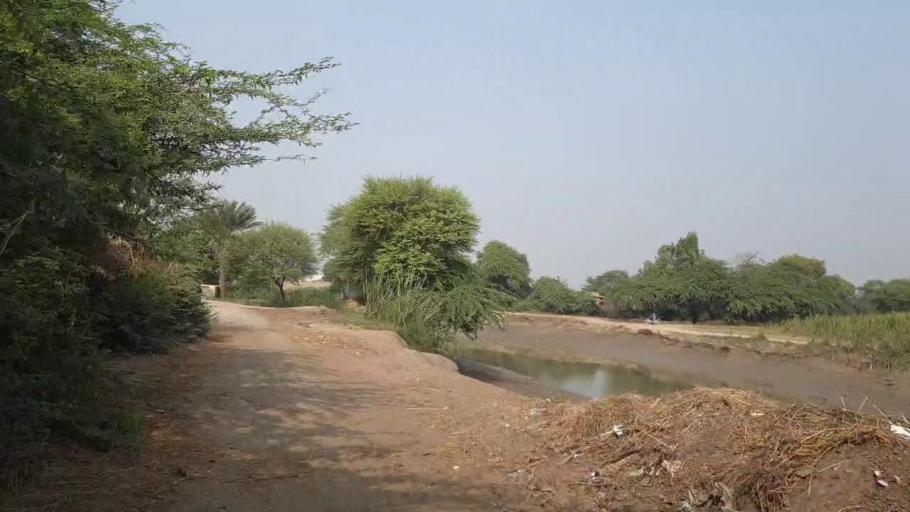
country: PK
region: Sindh
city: Matli
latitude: 25.0289
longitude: 68.5964
